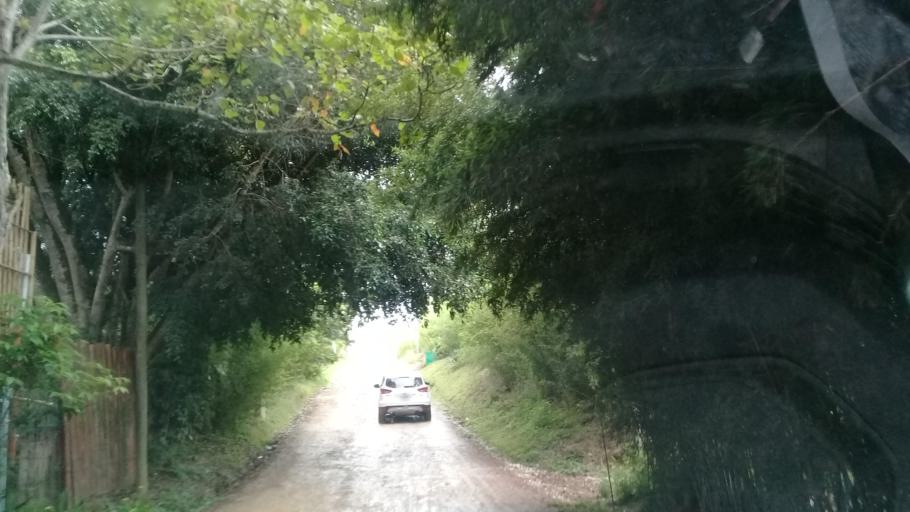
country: MX
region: Veracruz
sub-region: Emiliano Zapata
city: Jacarandas
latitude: 19.5058
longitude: -96.8438
